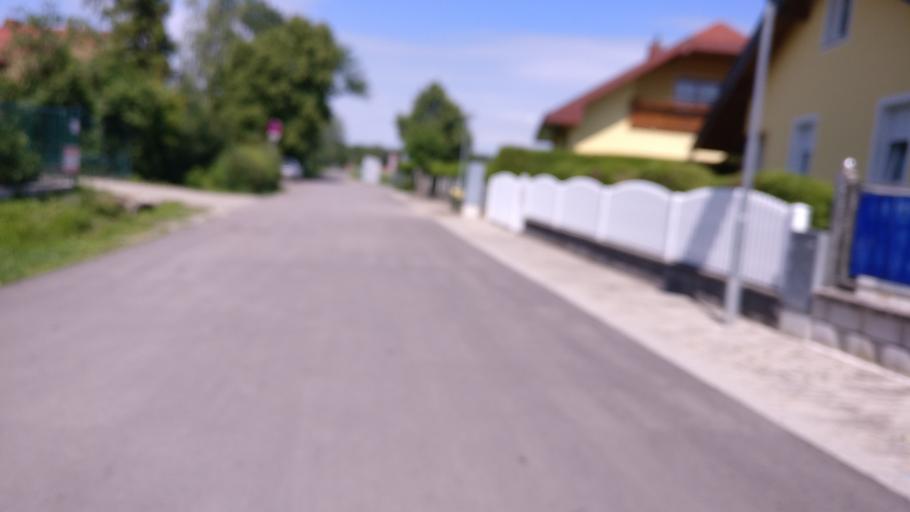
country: AT
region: Lower Austria
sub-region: Politischer Bezirk Baden
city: Gunselsdorf
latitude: 47.9421
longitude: 16.2627
